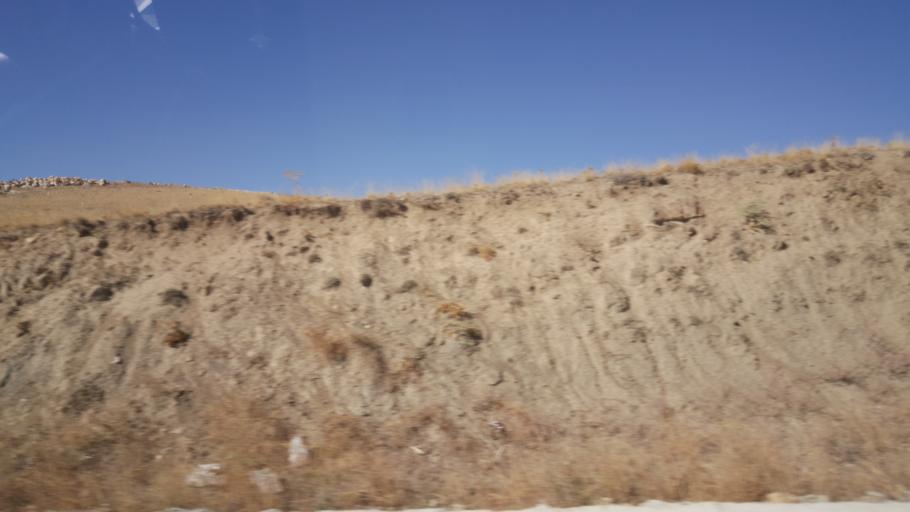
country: TR
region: Ankara
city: Ikizce
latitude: 39.6285
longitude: 32.7041
